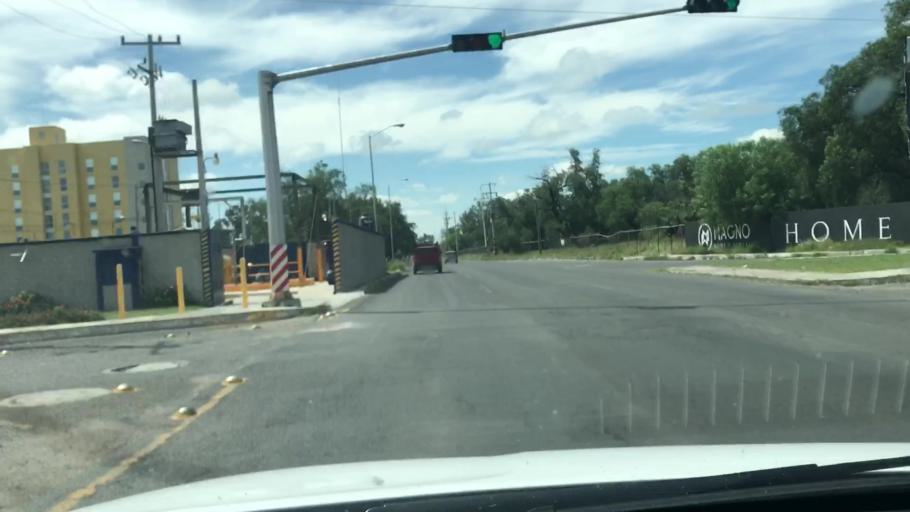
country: MX
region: Guanajuato
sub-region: Celaya
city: La Trinidad
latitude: 20.5303
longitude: -100.7766
